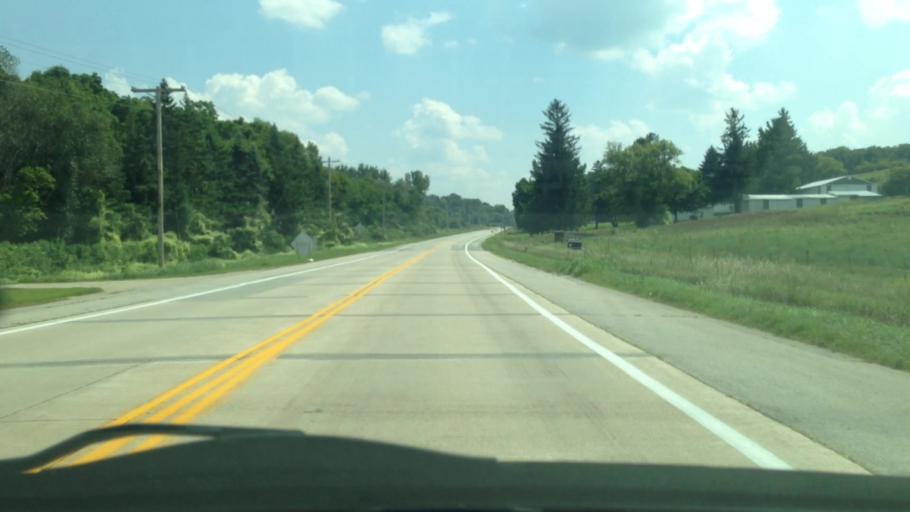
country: US
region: Minnesota
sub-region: Olmsted County
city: Rochester
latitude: 43.9707
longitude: -92.4368
